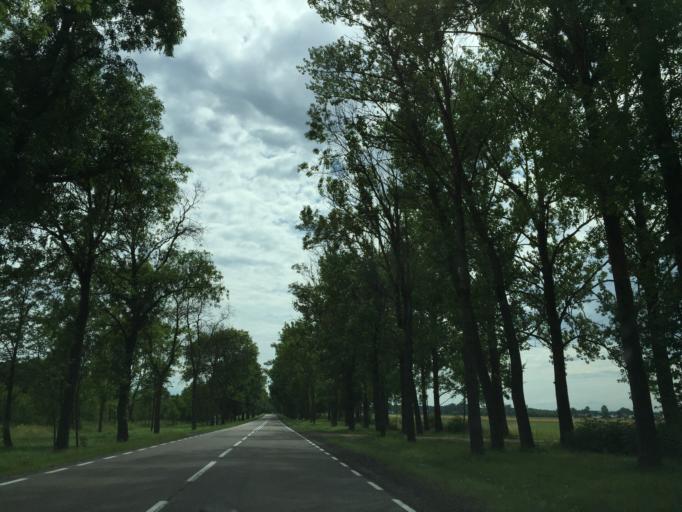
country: PL
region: Podlasie
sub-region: Powiat bielski
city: Bielsk Podlaski
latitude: 52.7087
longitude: 23.1351
